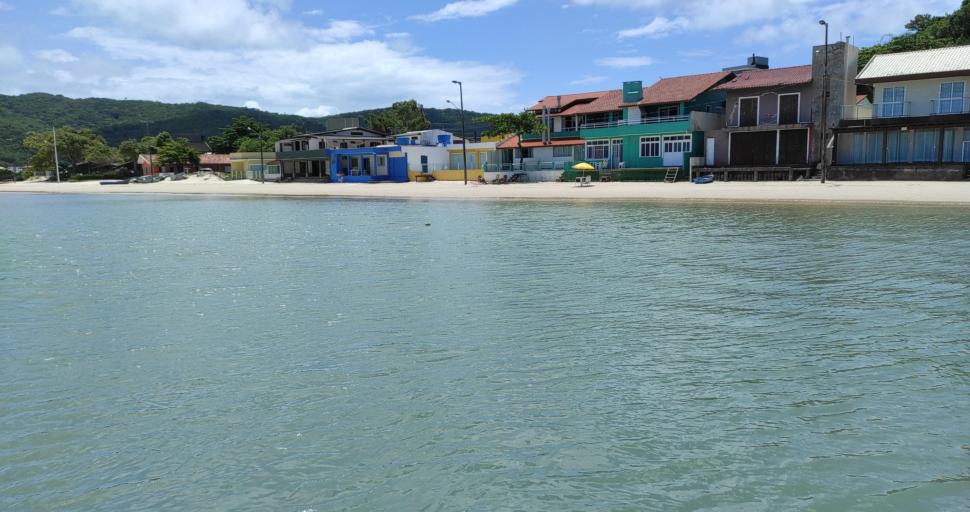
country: BR
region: Santa Catarina
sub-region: Porto Belo
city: Porto Belo
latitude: -27.1815
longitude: -48.5226
